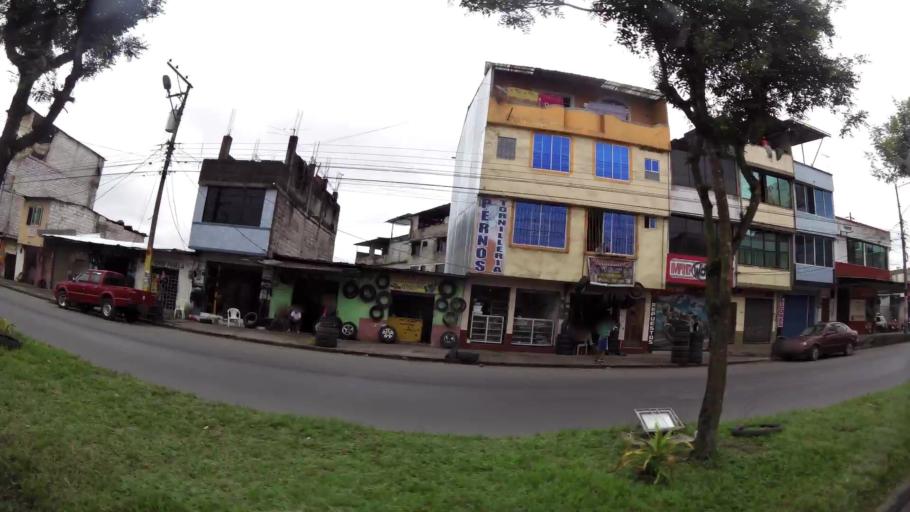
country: EC
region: Santo Domingo de los Tsachilas
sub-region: Canton Santo Domingo de los Colorados
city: Santo Domingo de los Colorados
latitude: -0.2424
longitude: -79.1712
